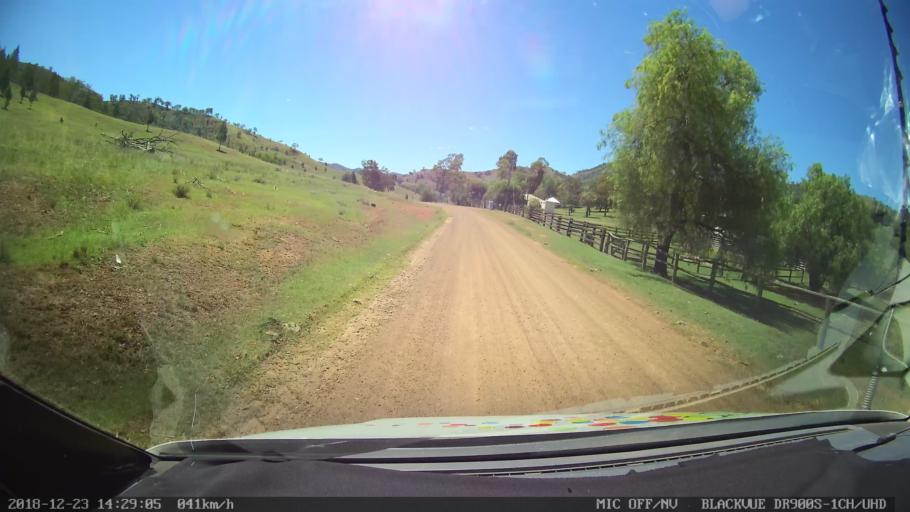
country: AU
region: New South Wales
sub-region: Tamworth Municipality
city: Manilla
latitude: -30.6109
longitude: 150.9393
